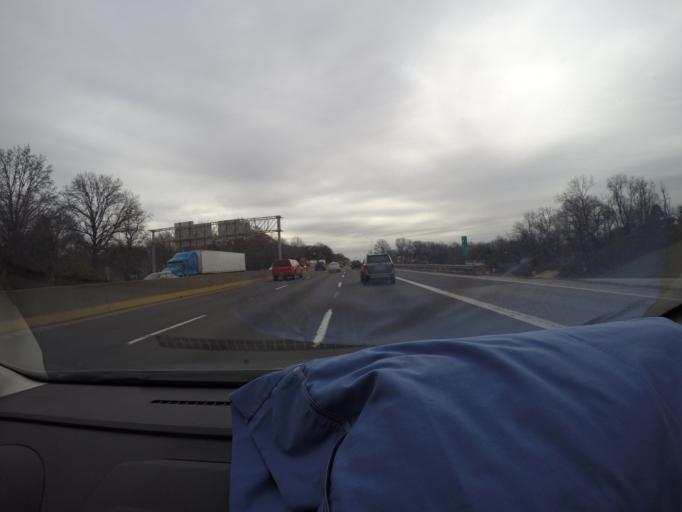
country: US
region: Missouri
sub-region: Saint Louis County
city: Northwoods
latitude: 38.7101
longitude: -90.2835
